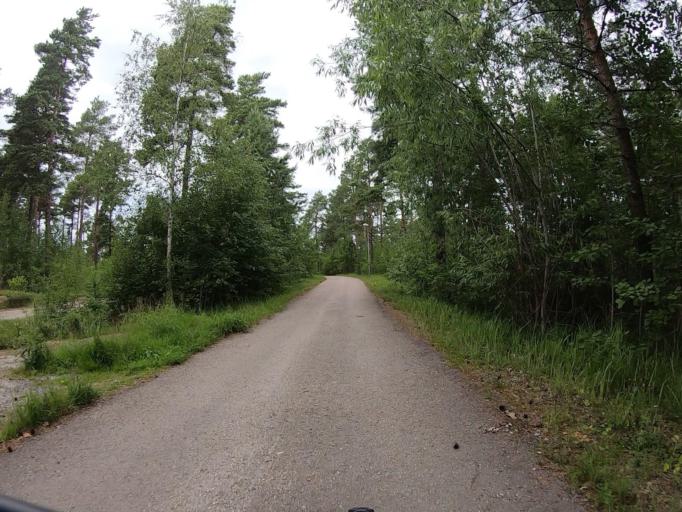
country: FI
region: Varsinais-Suomi
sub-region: Vakka-Suomi
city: Uusikaupunki
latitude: 60.8166
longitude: 21.4168
